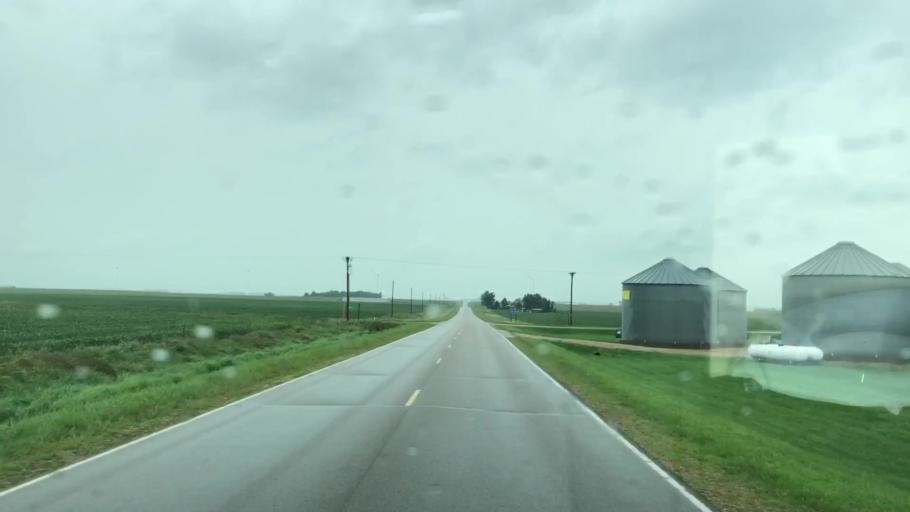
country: US
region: Iowa
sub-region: O'Brien County
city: Sanborn
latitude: 43.2166
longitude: -95.7234
